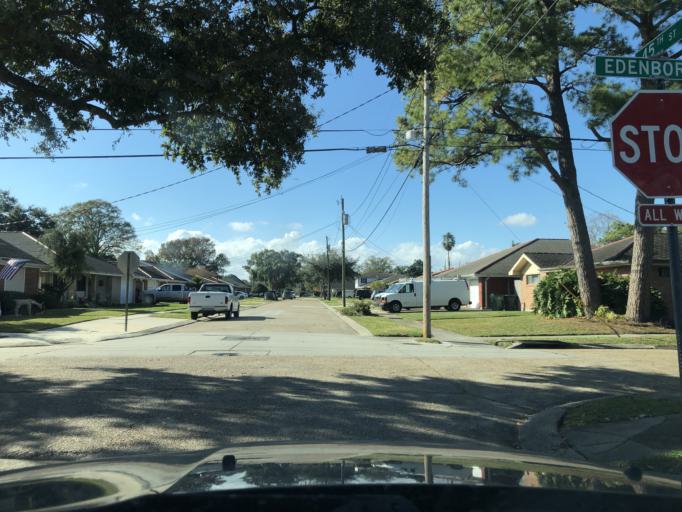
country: US
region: Louisiana
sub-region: Jefferson Parish
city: Metairie Terrace
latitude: 29.9862
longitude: -90.1626
